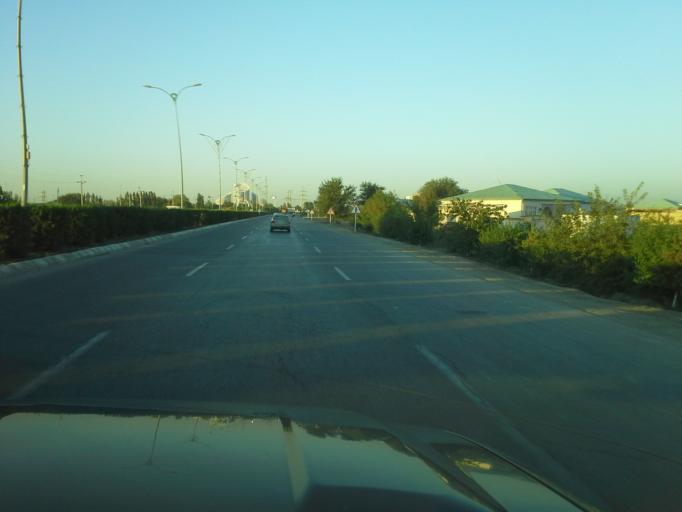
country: TM
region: Dasoguz
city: Dasoguz
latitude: 41.8179
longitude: 59.9190
